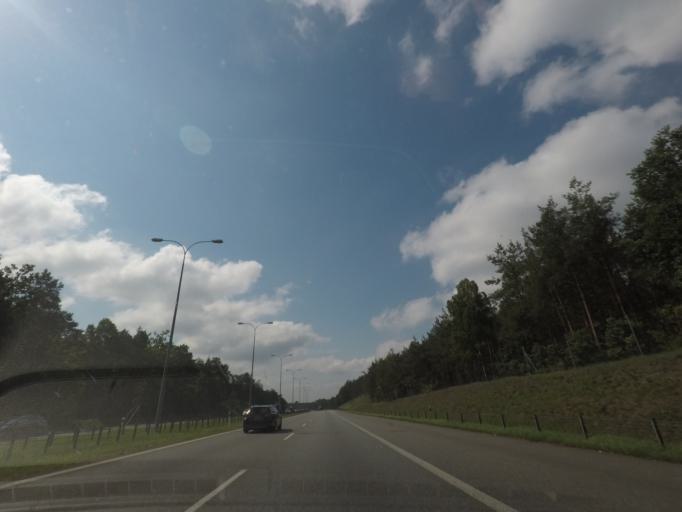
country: PL
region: Kujawsko-Pomorskie
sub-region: Powiat torunski
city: Lubicz Dolny
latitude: 53.0081
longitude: 18.7336
